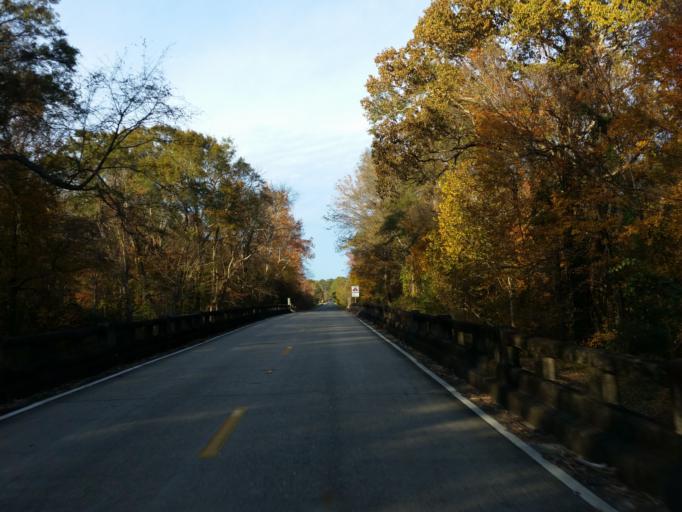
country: US
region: Mississippi
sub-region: Clarke County
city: Stonewall
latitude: 32.0628
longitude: -88.8802
